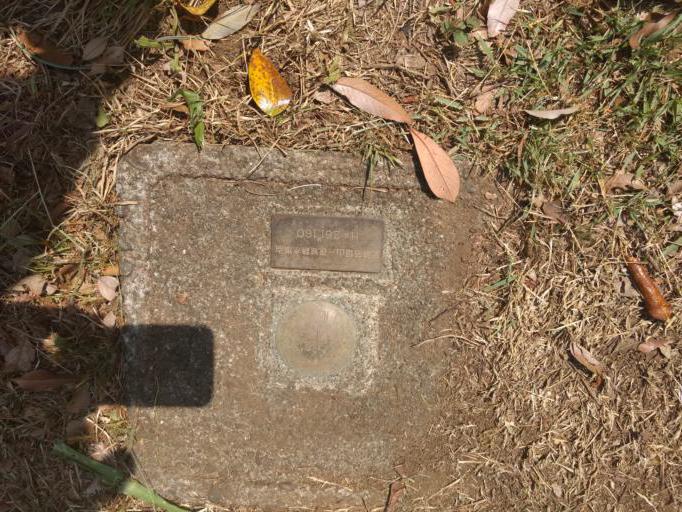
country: JP
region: Kanagawa
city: Odawara
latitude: 35.2350
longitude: 139.1271
